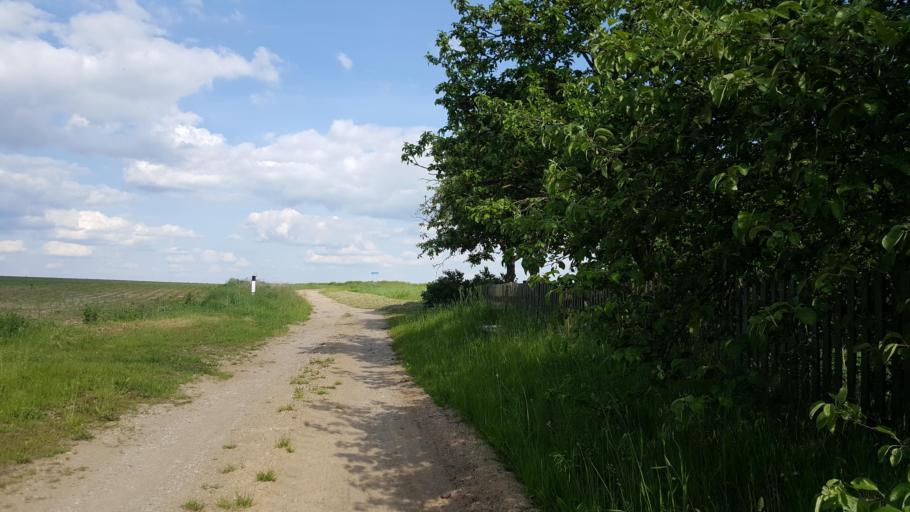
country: BY
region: Brest
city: Kamyanyets
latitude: 52.4181
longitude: 23.6658
